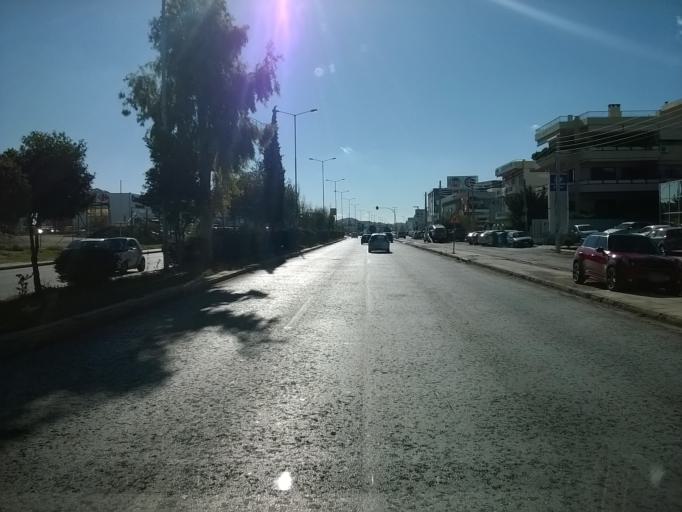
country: GR
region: Attica
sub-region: Nomarchia Athinas
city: Glyfada
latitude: 37.8734
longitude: 23.7576
